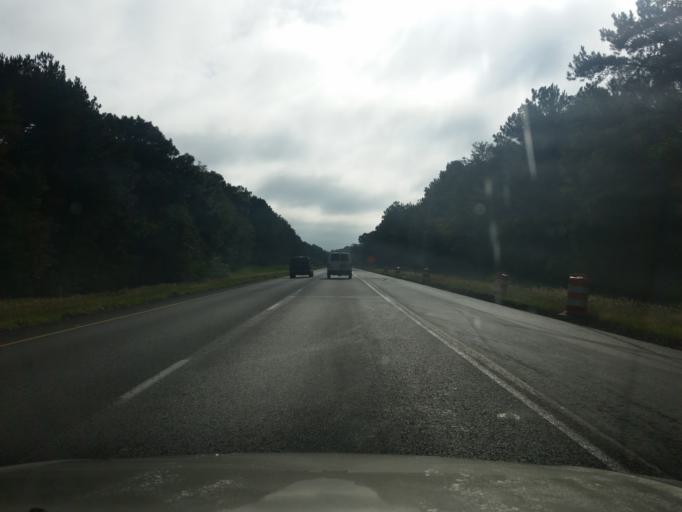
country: US
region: Alabama
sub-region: Baldwin County
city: Loxley
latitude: 30.6542
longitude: -87.7986
